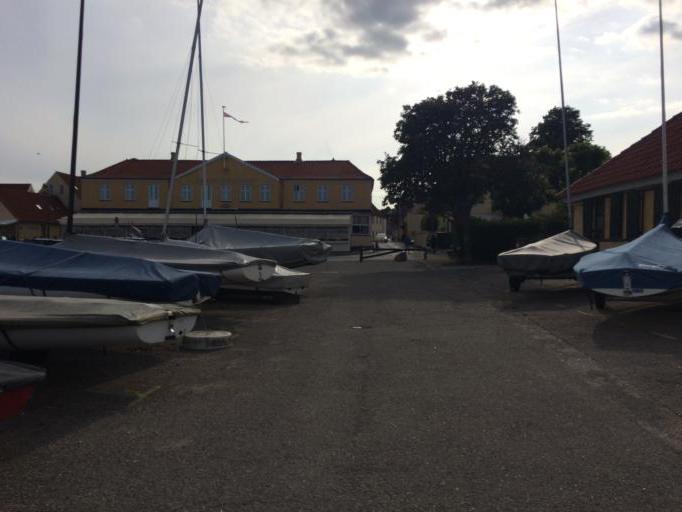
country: DK
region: Capital Region
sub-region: Dragor Kommune
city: Dragor
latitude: 55.5944
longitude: 12.6751
